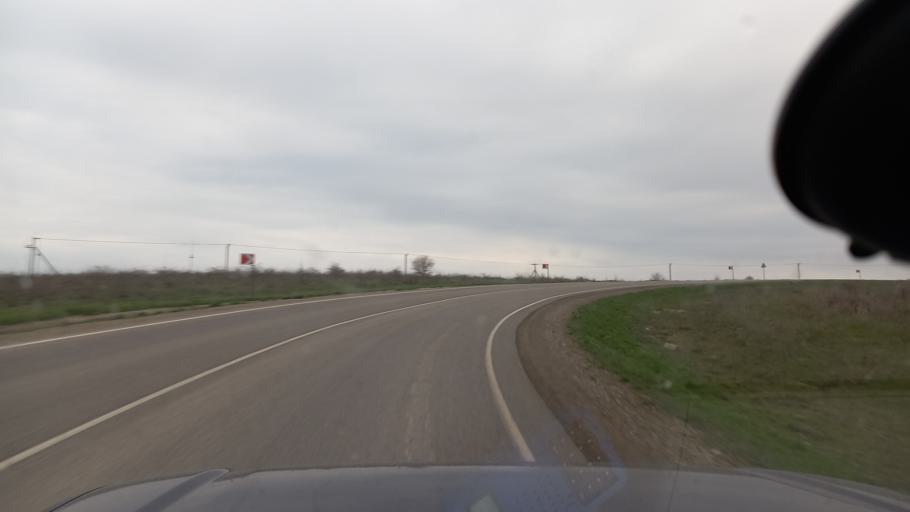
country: RU
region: Krasnodarskiy
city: Sukko
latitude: 44.8382
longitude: 37.4298
